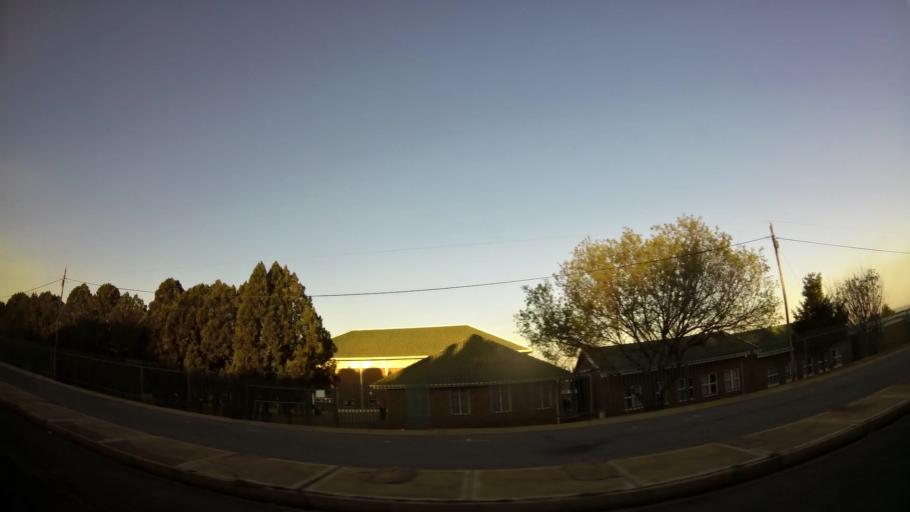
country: ZA
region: Gauteng
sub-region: City of Johannesburg Metropolitan Municipality
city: Roodepoort
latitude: -26.1494
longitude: 27.8940
